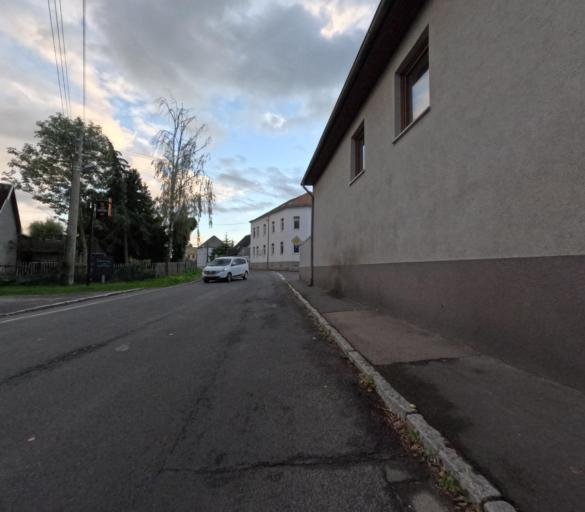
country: DE
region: Saxony
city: Markranstadt
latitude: 51.2725
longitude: 12.2321
